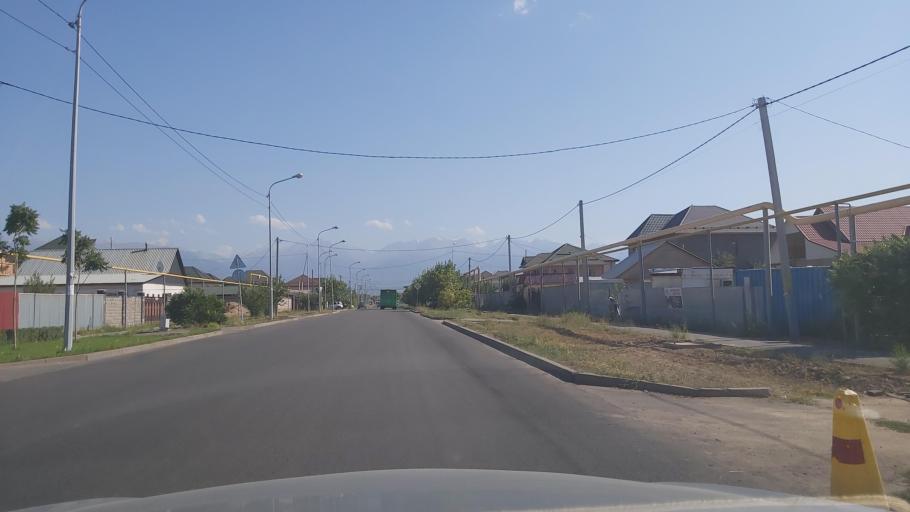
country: KZ
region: Almaty Oblysy
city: Burunday
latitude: 43.3182
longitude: 76.8417
